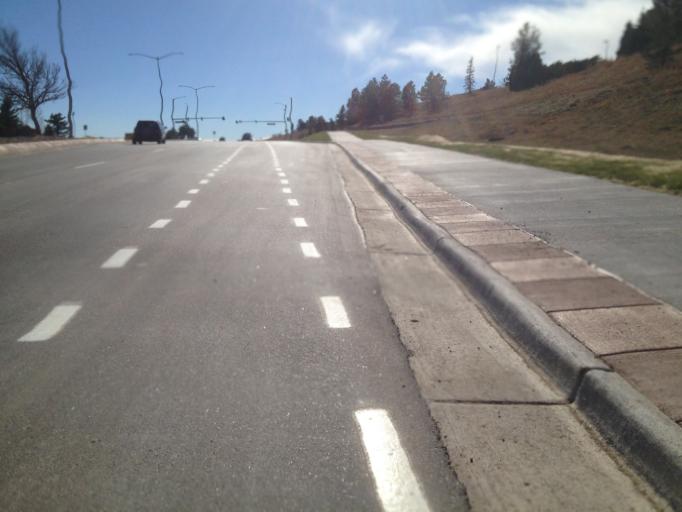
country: US
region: Colorado
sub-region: Boulder County
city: Superior
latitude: 39.9468
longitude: -105.1642
